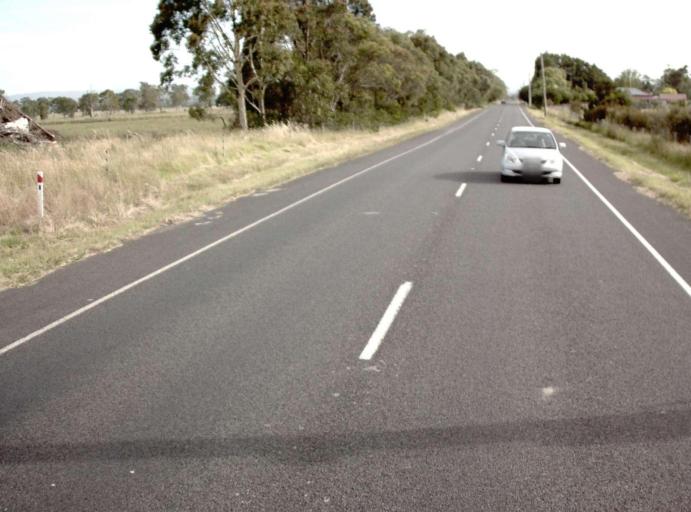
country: AU
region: Victoria
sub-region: Latrobe
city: Traralgon
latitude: -38.1354
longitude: 146.5578
